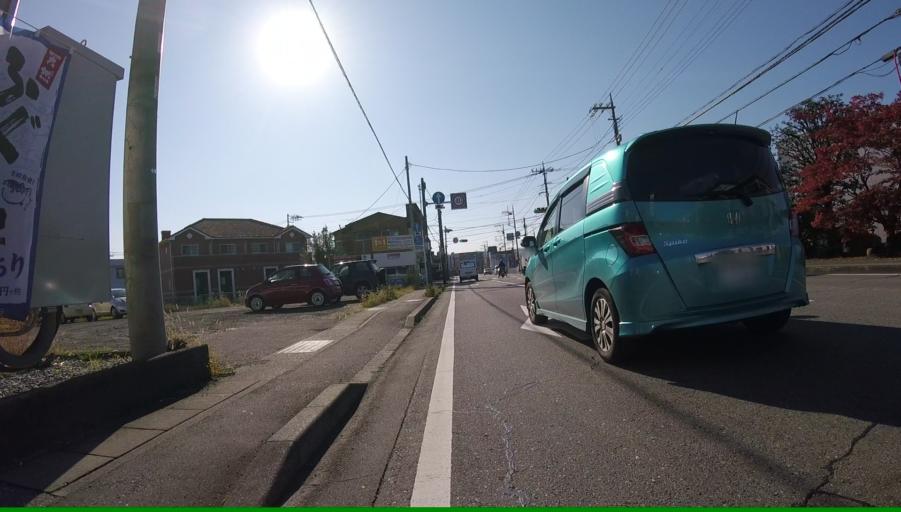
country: JP
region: Shizuoka
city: Mishima
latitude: 35.1059
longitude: 138.9159
